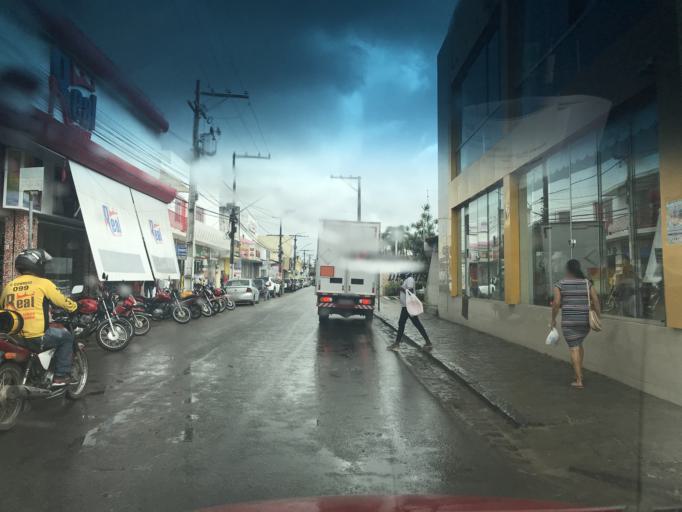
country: BR
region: Bahia
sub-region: Cruz Das Almas
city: Cruz das Almas
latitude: -12.6727
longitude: -39.1028
